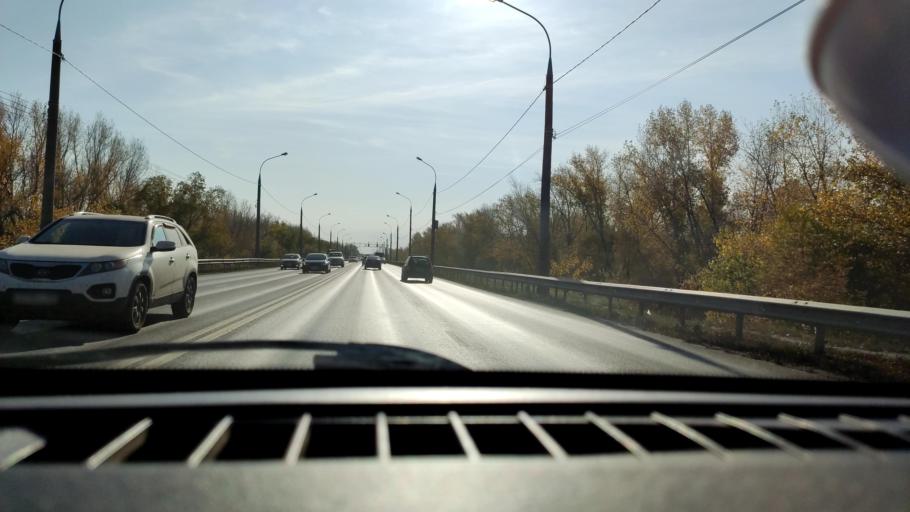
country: RU
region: Samara
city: Samara
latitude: 53.1520
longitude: 50.1874
